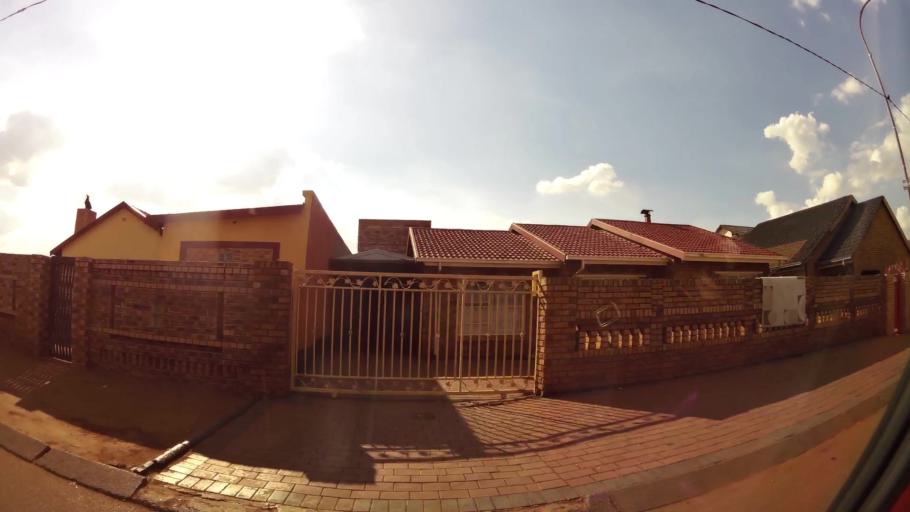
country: ZA
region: Gauteng
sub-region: City of Johannesburg Metropolitan Municipality
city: Soweto
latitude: -26.2223
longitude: 27.8622
